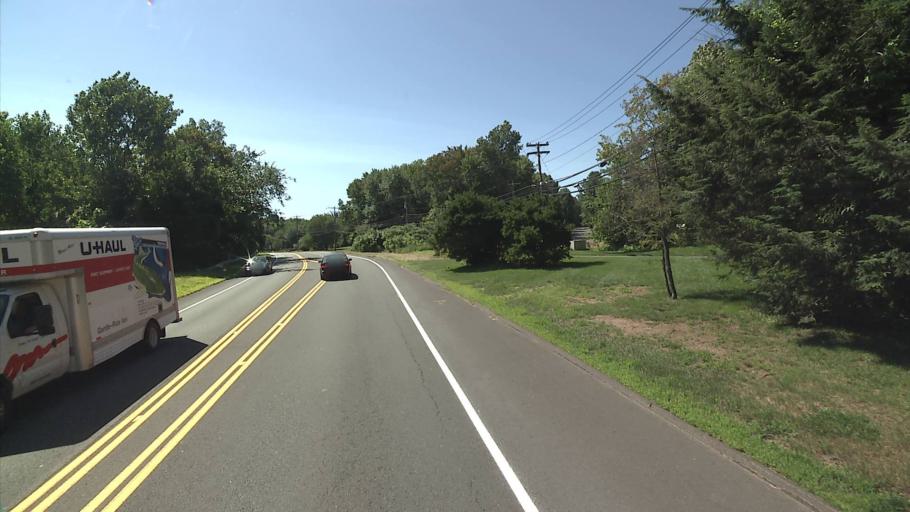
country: US
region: Connecticut
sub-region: Hartford County
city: Salmon Brook
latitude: 41.9379
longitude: -72.7931
